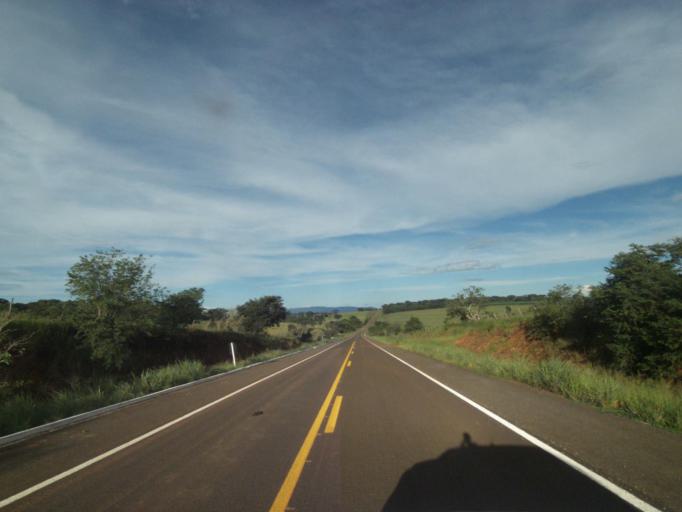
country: BR
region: Goias
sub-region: Jaragua
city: Jaragua
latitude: -15.8949
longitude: -49.4962
